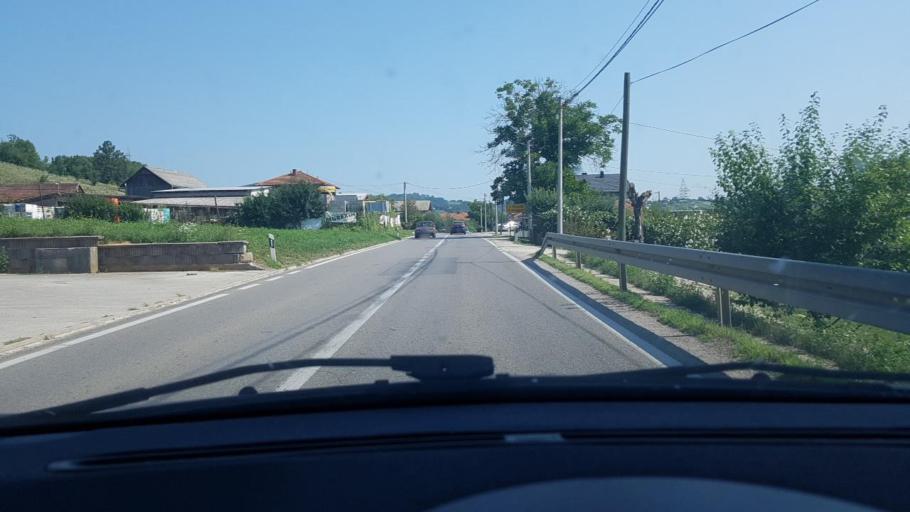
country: BA
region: Federation of Bosnia and Herzegovina
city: Velika Kladusa
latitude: 45.1736
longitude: 15.8193
